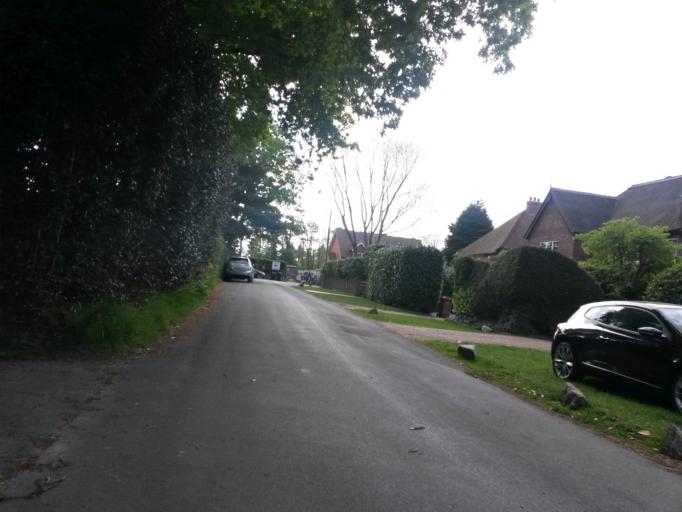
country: GB
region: England
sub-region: Surrey
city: Haslemere
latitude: 51.0837
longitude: -0.7108
